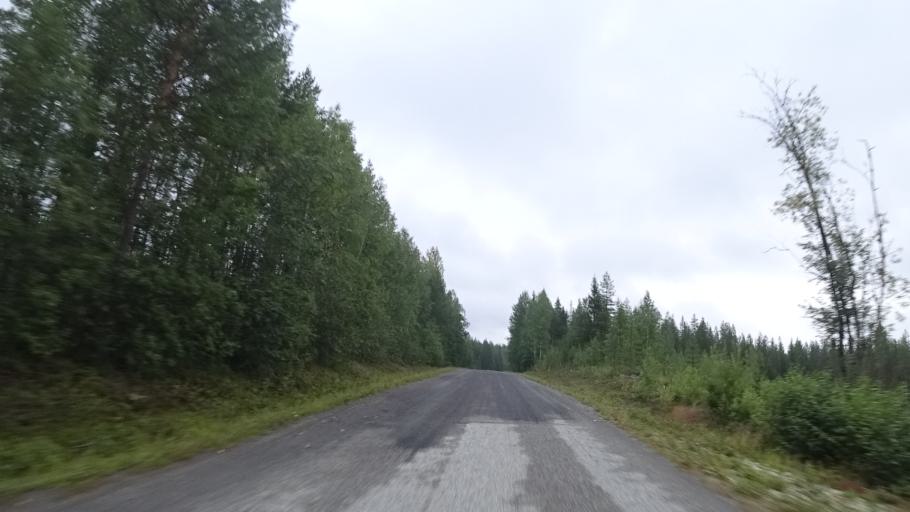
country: FI
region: North Karelia
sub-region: Joensuu
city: Ilomantsi
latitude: 63.2275
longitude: 30.8348
